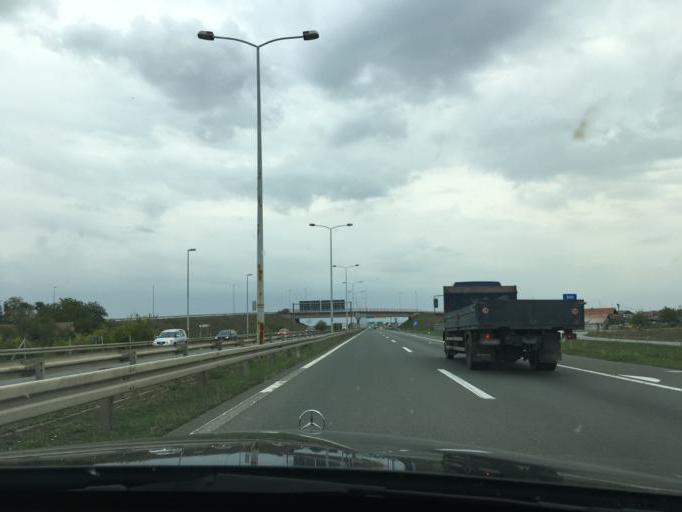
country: RS
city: Dobanovci
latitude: 44.8450
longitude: 20.2082
